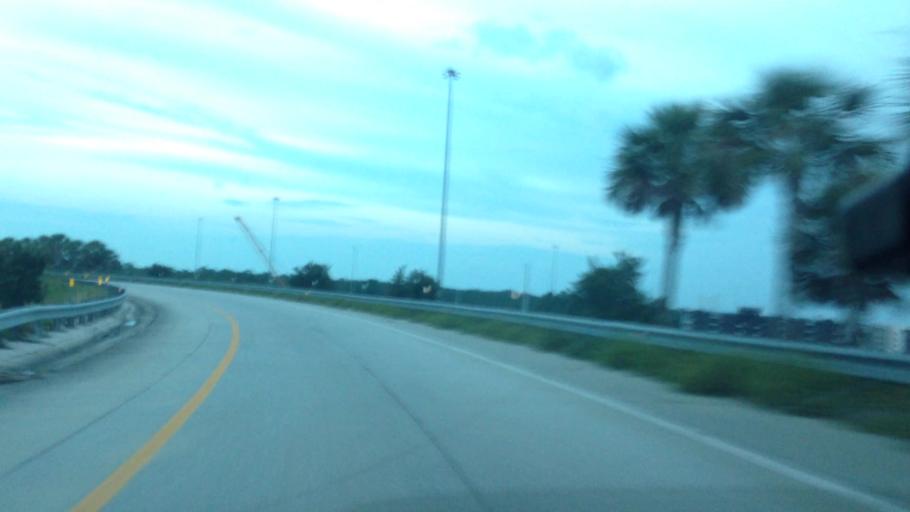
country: US
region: Florida
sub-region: Duval County
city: Jacksonville Beach
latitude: 30.2515
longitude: -81.5185
